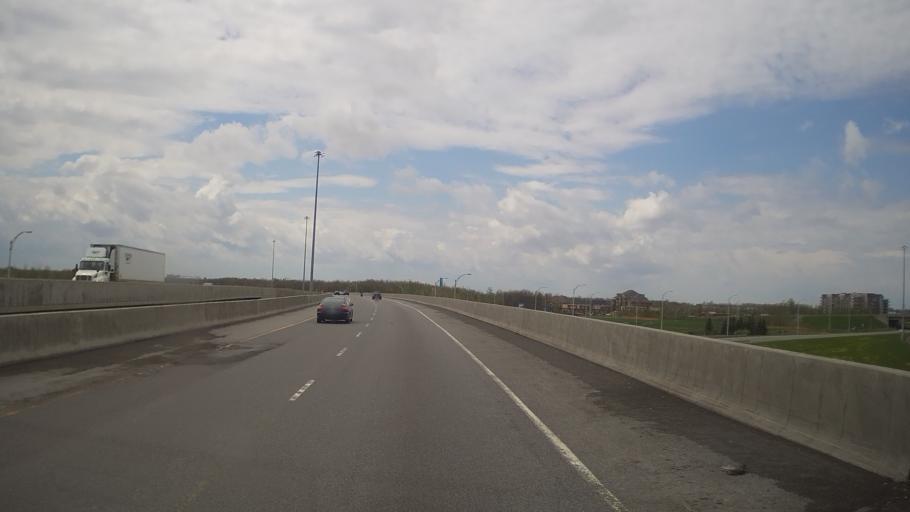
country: CA
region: Quebec
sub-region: Monteregie
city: Candiac
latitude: 45.3735
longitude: -73.4996
